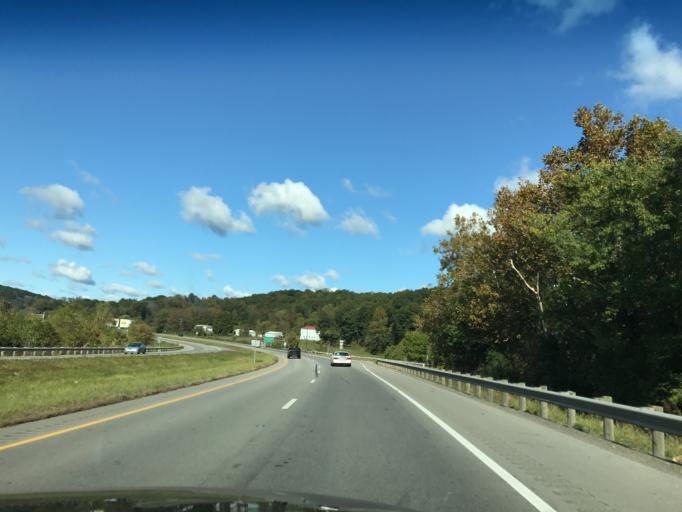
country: US
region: Ohio
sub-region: Athens County
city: Chauncey
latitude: 39.3890
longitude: -82.1431
